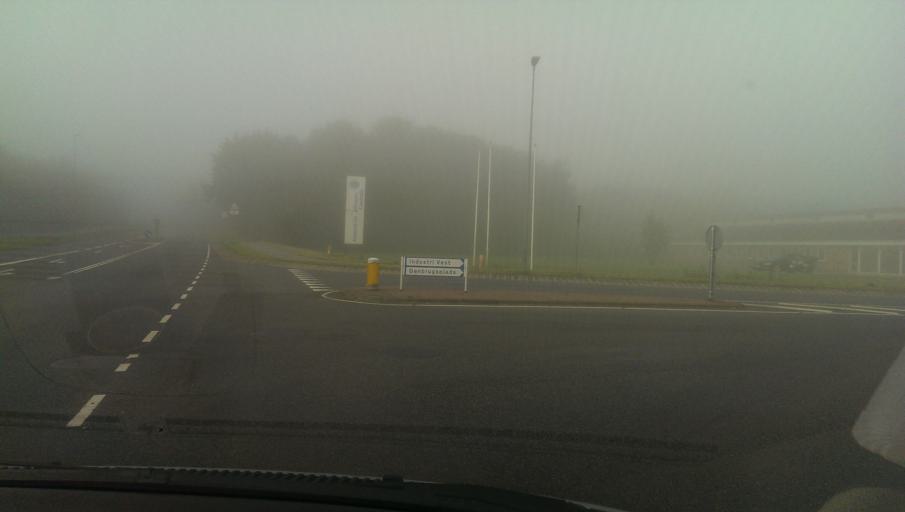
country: DK
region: South Denmark
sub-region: Vejen Kommune
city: Vejen
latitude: 55.4886
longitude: 9.1289
